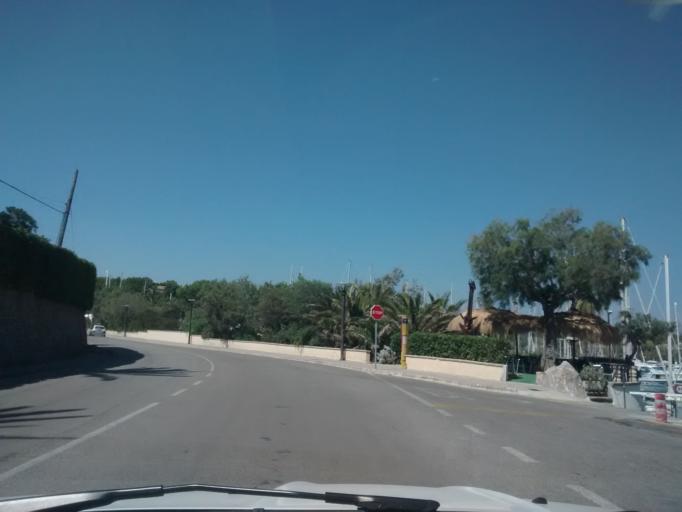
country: ES
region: Balearic Islands
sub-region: Illes Balears
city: Port d'Alcudia
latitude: 39.8660
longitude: 3.1462
